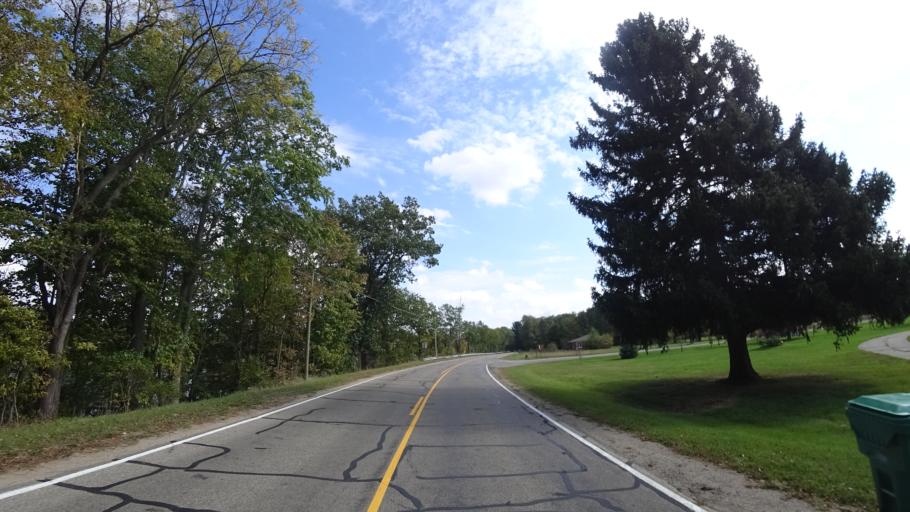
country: US
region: Michigan
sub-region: Saint Joseph County
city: Three Rivers
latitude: 41.9402
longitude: -85.6061
